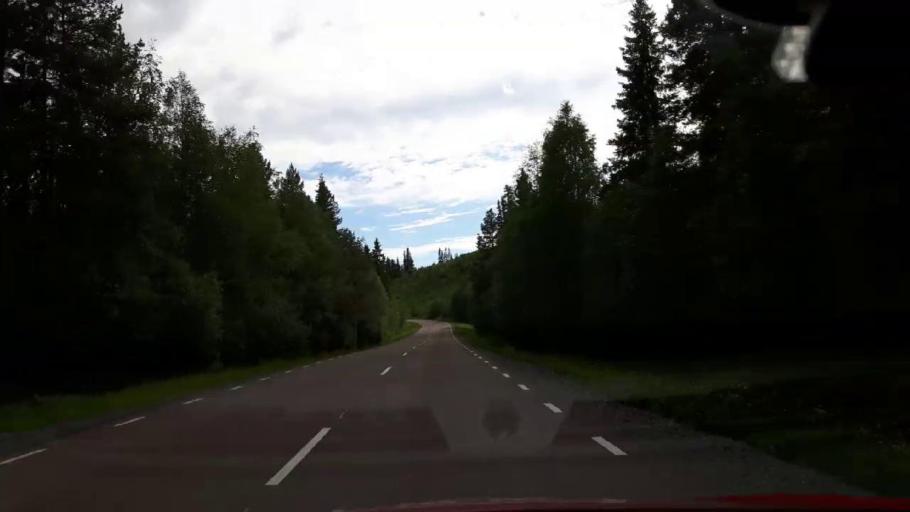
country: SE
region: Jaemtland
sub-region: Krokoms Kommun
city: Valla
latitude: 63.9409
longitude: 14.2233
